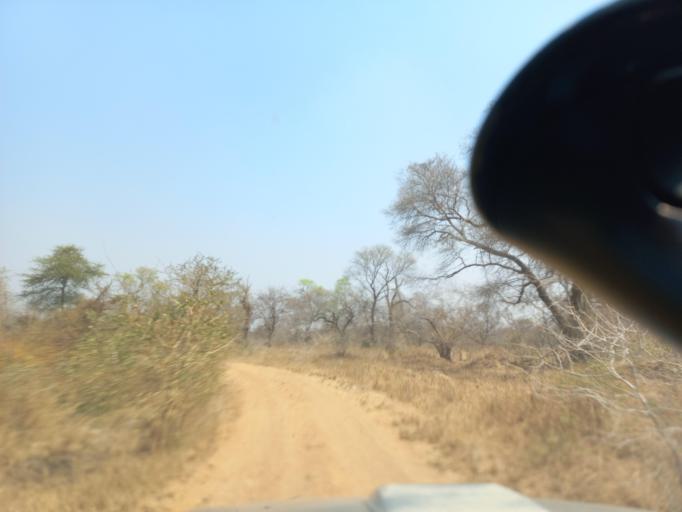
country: ZW
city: Chirundu
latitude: -15.9327
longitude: 28.7208
